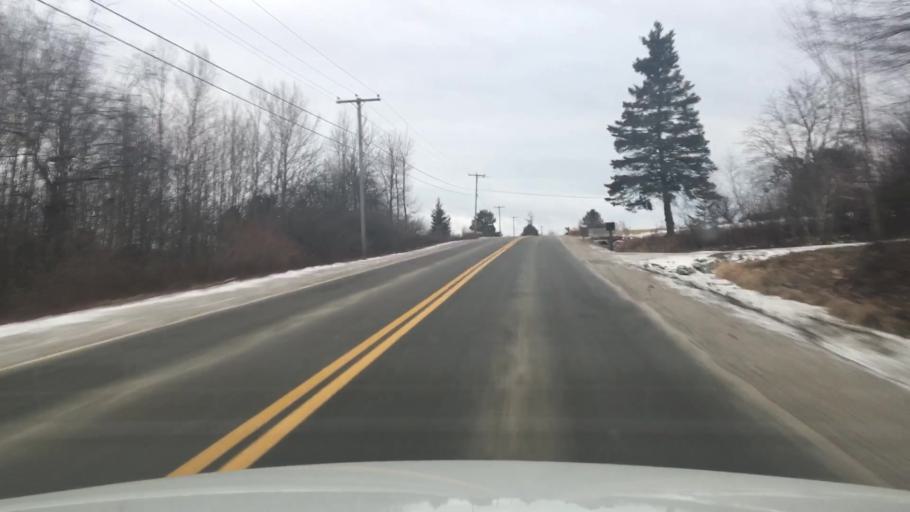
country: US
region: Maine
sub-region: Hancock County
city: Trenton
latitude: 44.4944
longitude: -68.3630
